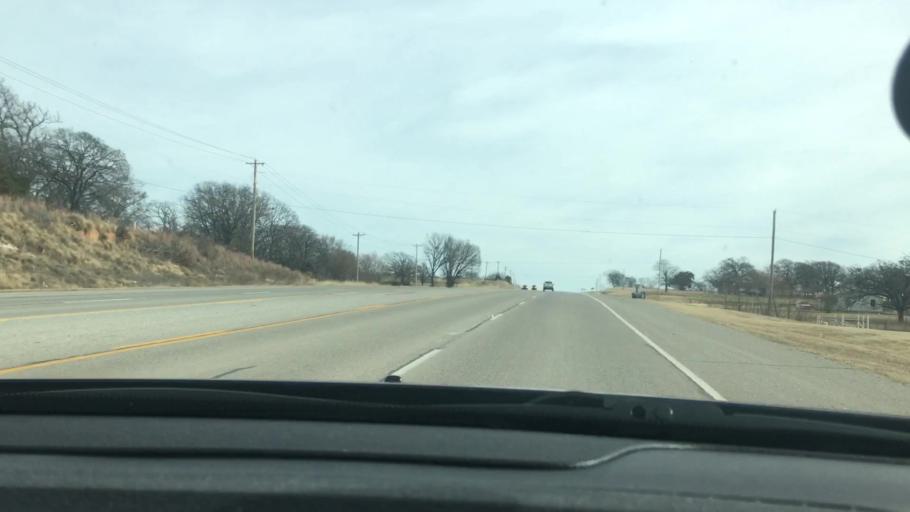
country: US
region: Oklahoma
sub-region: Carter County
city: Dickson
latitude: 34.1871
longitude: -97.0276
